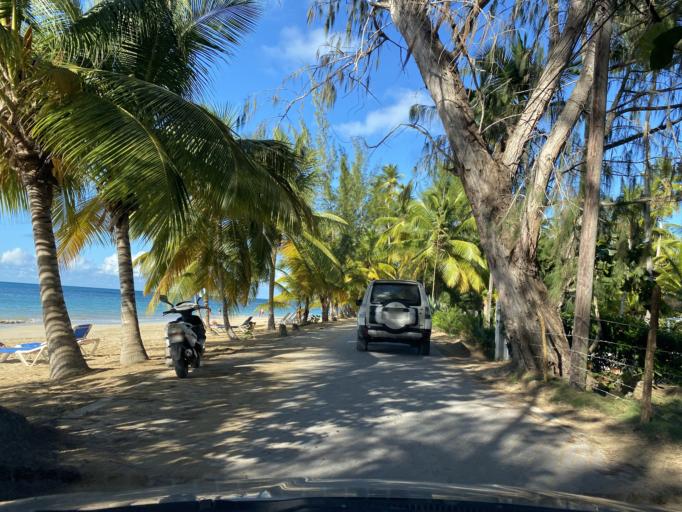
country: DO
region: Samana
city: Las Terrenas
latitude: 19.3213
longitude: -69.5550
